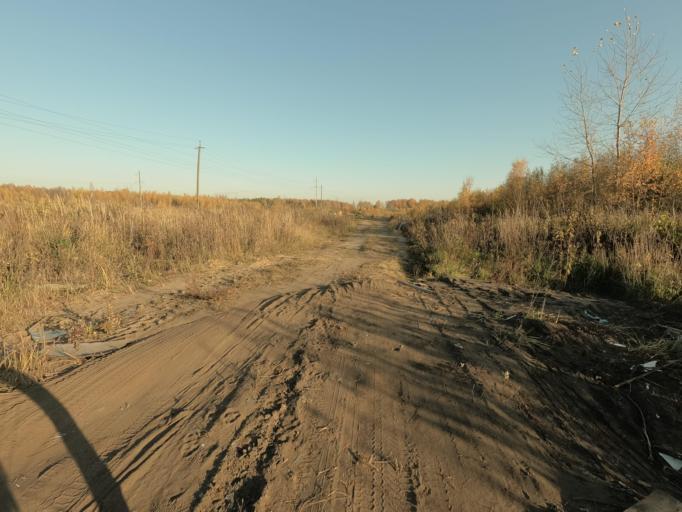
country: RU
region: Leningrad
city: Kirovsk
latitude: 59.8617
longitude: 31.0123
